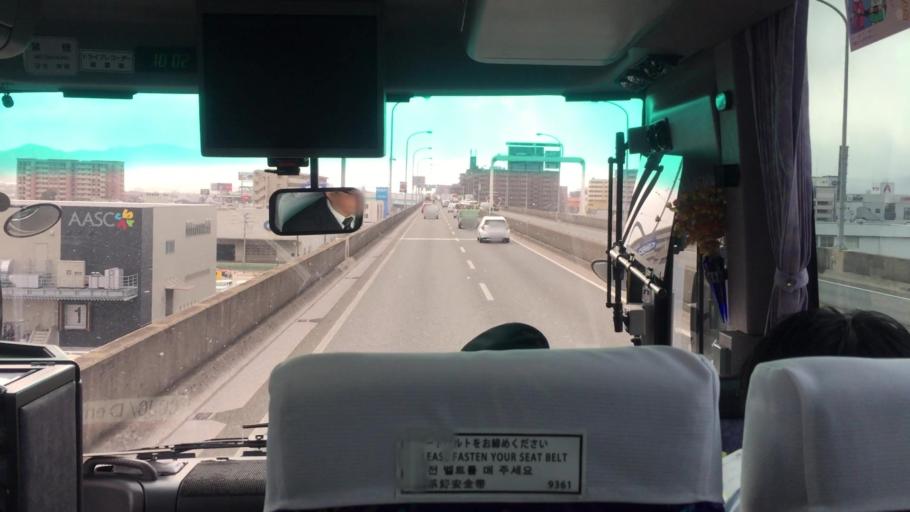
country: JP
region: Fukuoka
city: Fukuoka-shi
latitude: 33.5807
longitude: 130.4436
